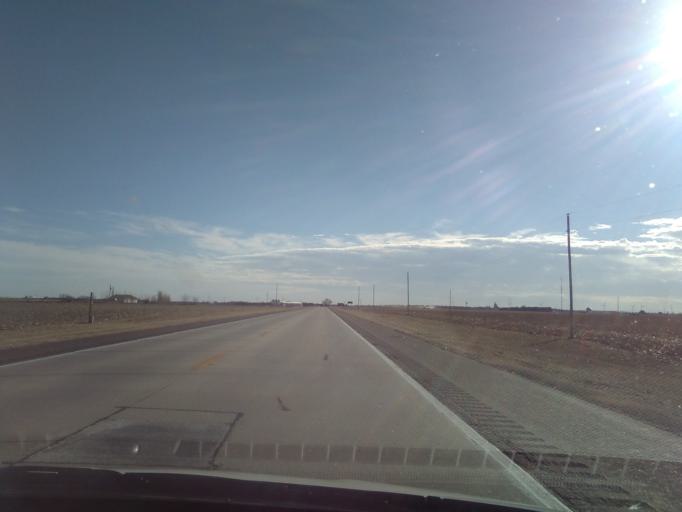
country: US
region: Nebraska
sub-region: Adams County
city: Hastings
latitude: 40.3679
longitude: -98.4398
